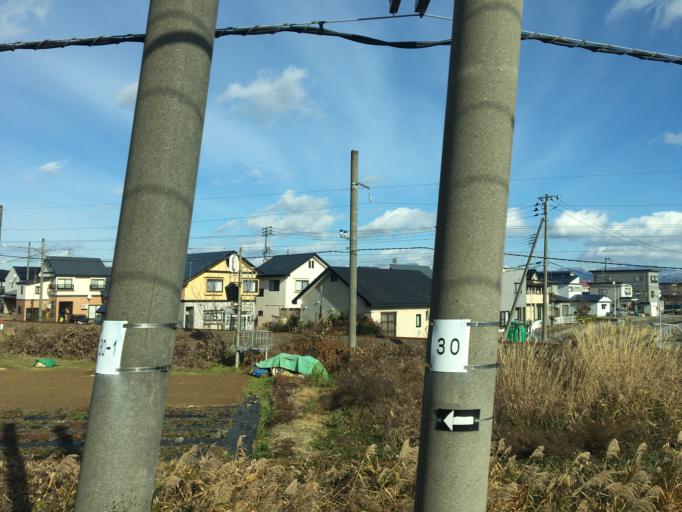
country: JP
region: Akita
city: Omagari
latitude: 39.4698
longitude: 140.4754
